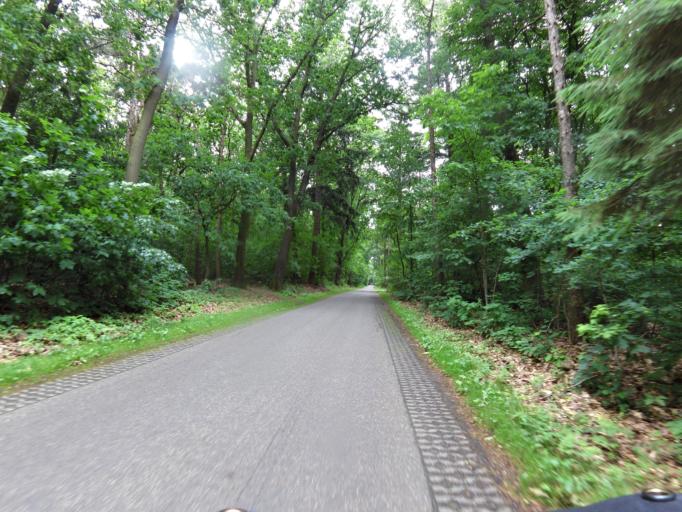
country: NL
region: Gelderland
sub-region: Gemeente Apeldoorn
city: Uddel
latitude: 52.2870
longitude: 5.7959
